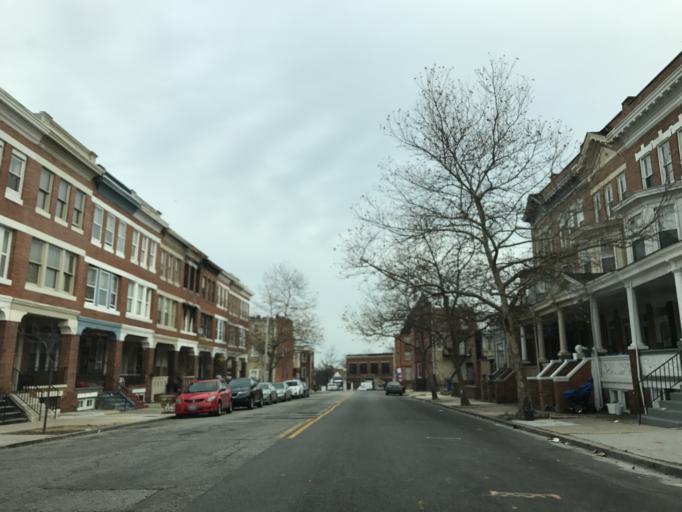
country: US
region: Maryland
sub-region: City of Baltimore
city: Baltimore
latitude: 39.3144
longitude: -76.6328
